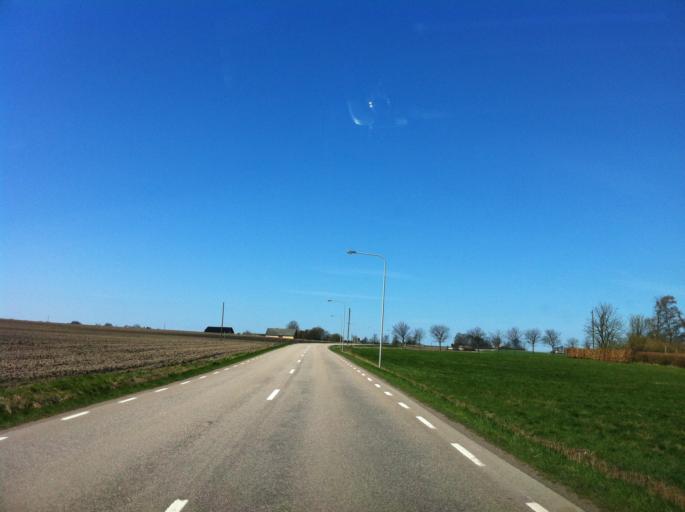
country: SE
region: Skane
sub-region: Helsingborg
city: Glumslov
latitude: 55.9270
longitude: 12.8741
